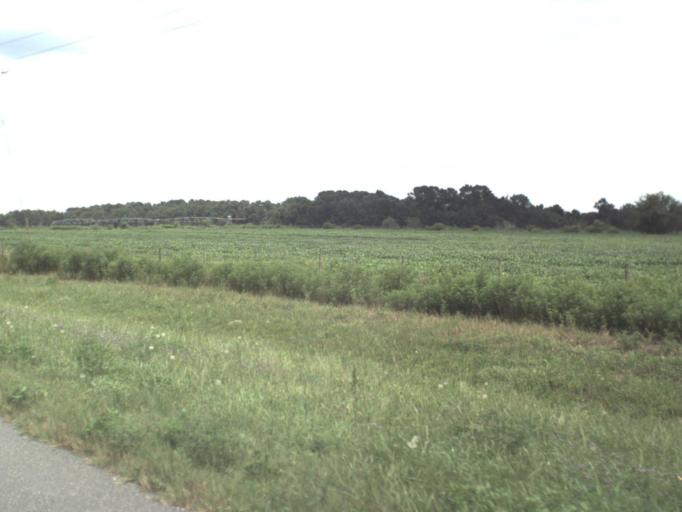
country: US
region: Florida
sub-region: Alachua County
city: Alachua
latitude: 29.8401
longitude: -82.3595
